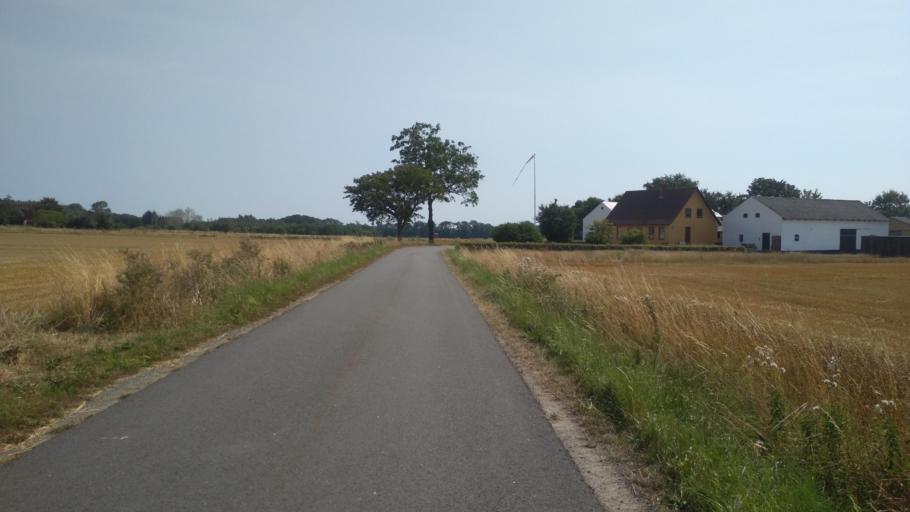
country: DK
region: Capital Region
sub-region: Bornholm Kommune
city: Akirkeby
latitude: 55.0544
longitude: 14.9385
